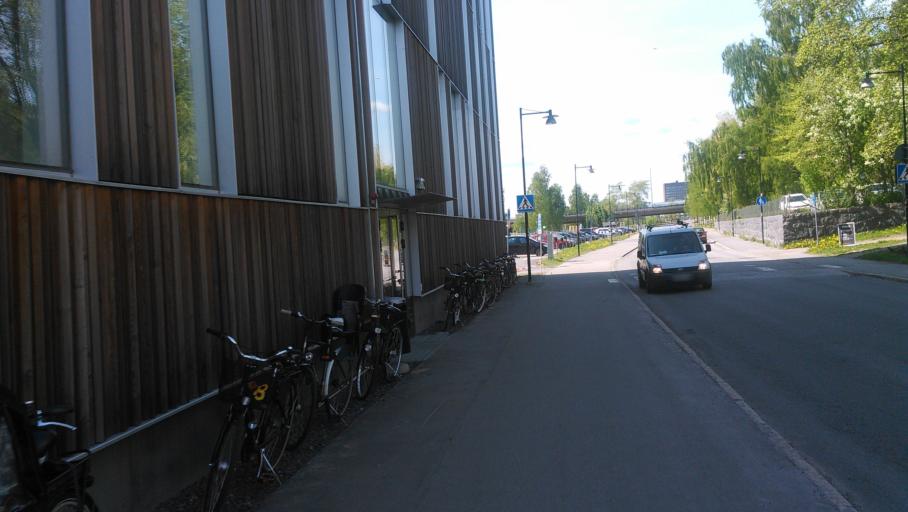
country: SE
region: Vaesterbotten
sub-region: Umea Kommun
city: Umea
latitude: 63.8214
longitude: 20.2736
